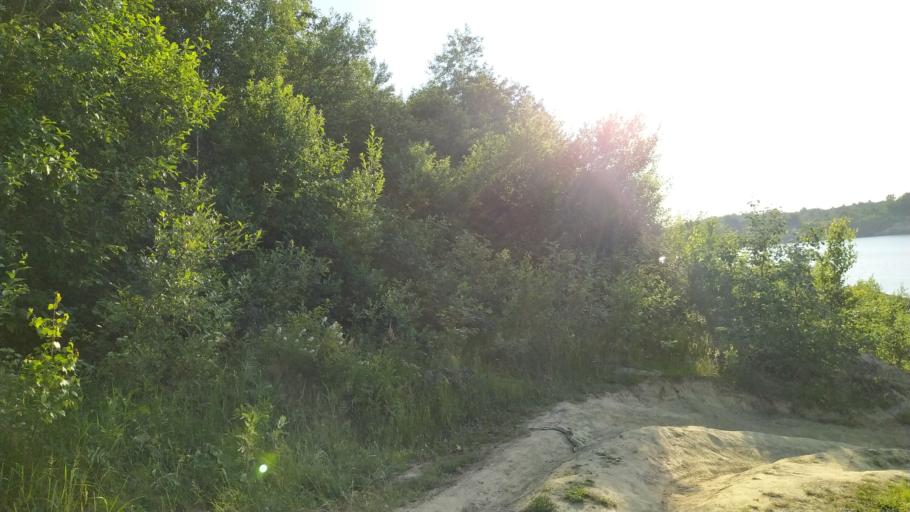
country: RU
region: Leningrad
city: Toksovo
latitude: 60.1134
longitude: 30.5472
